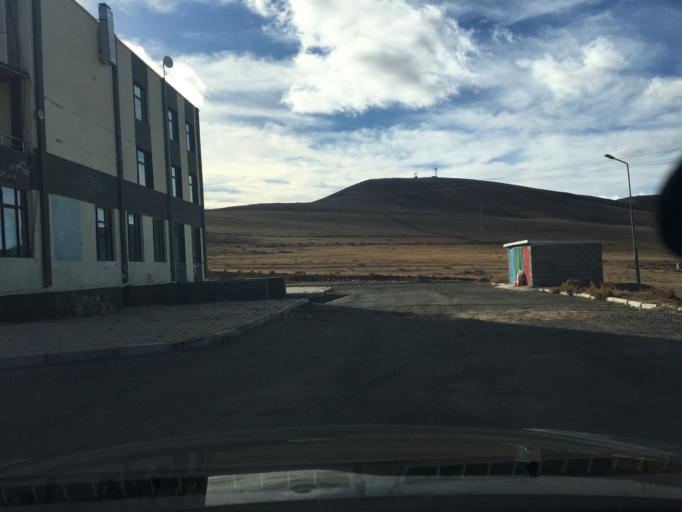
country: MN
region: Ulaanbaatar
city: Ulaanbaatar
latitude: 47.7900
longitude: 106.7453
